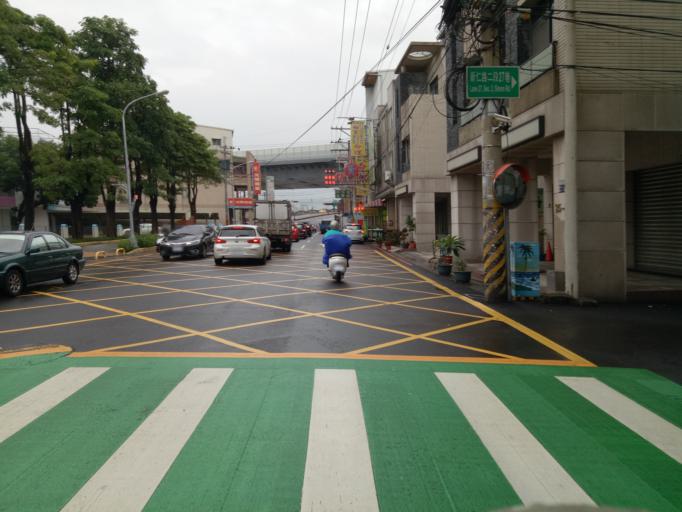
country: TW
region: Taiwan
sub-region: Taichung City
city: Taichung
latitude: 24.1112
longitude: 120.6957
